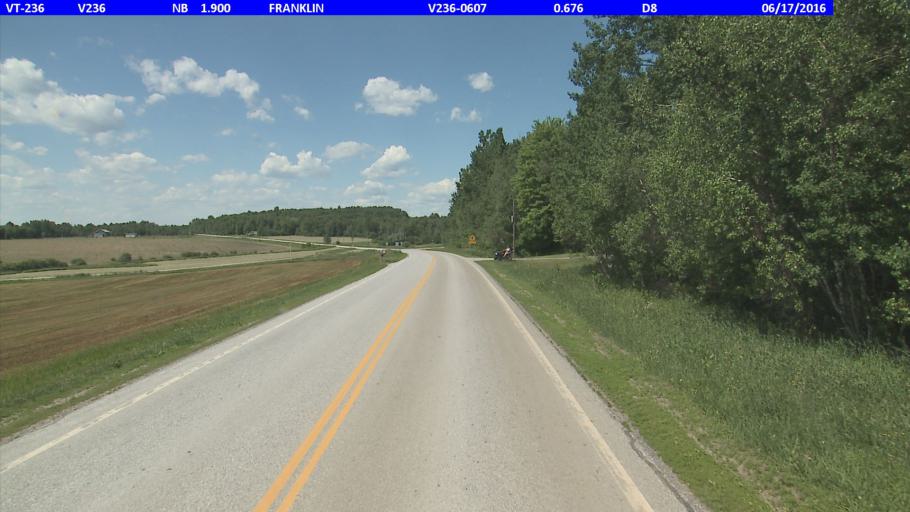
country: US
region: Vermont
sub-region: Franklin County
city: Enosburg Falls
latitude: 44.9379
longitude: -72.8629
